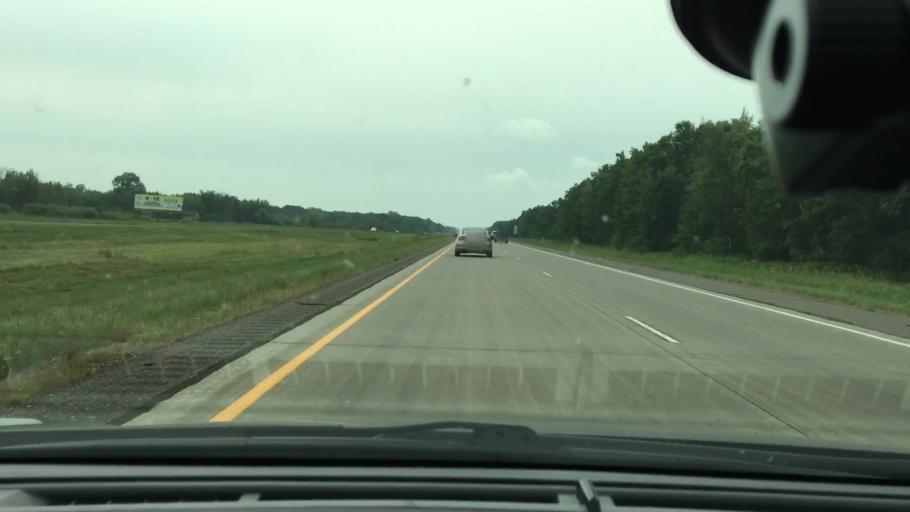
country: US
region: Minnesota
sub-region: Mille Lacs County
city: Vineland
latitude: 46.0314
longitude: -93.6630
